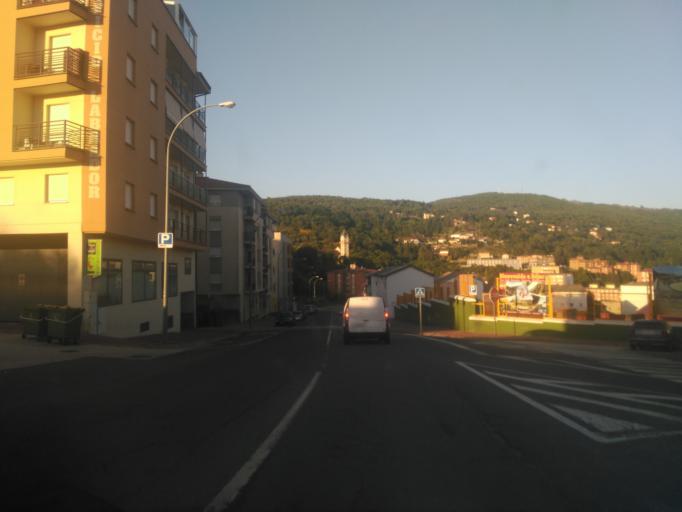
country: ES
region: Castille and Leon
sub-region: Provincia de Salamanca
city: Bejar
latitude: 40.3883
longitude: -5.7521
